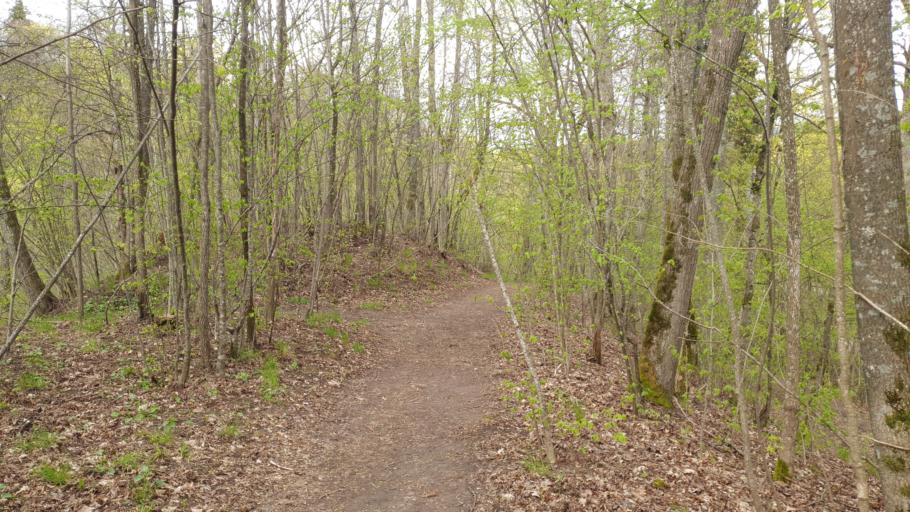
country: LT
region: Kauno apskritis
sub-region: Kauno rajonas
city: Akademija (Kaunas)
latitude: 54.9458
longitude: 23.7857
